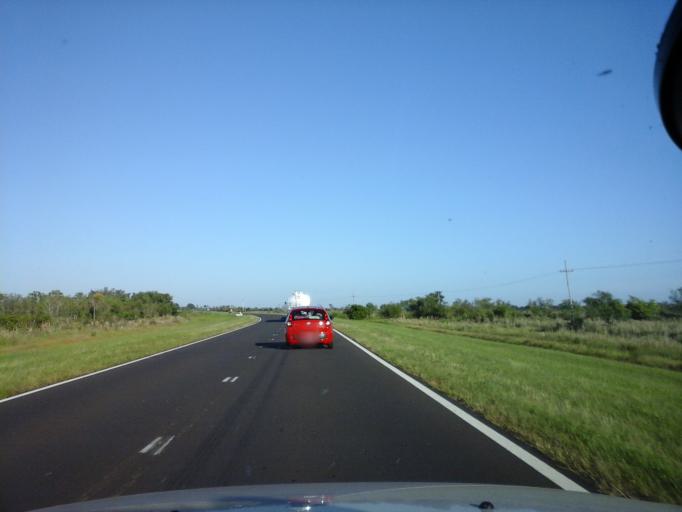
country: AR
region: Corrientes
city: Ita Ibate
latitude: -27.5034
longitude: -57.2477
